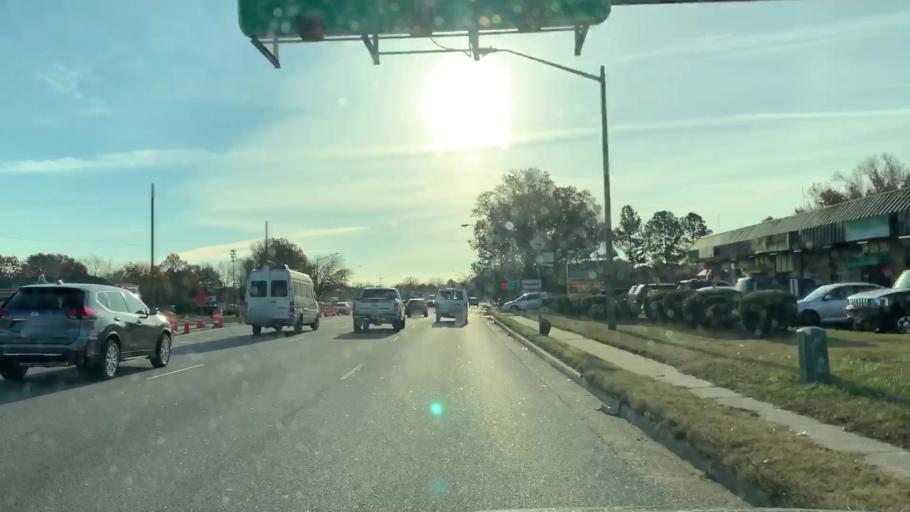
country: US
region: Virginia
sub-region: City of Chesapeake
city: Chesapeake
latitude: 36.7966
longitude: -76.1740
